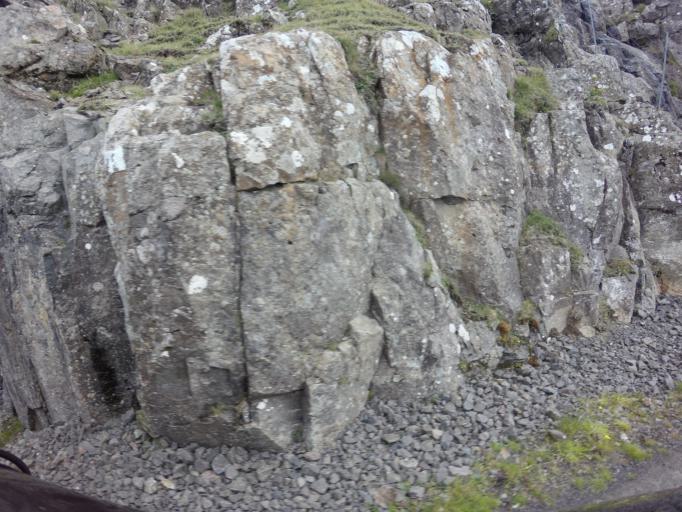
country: FO
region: Sandoy
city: Sandur
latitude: 61.8032
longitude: -6.7526
